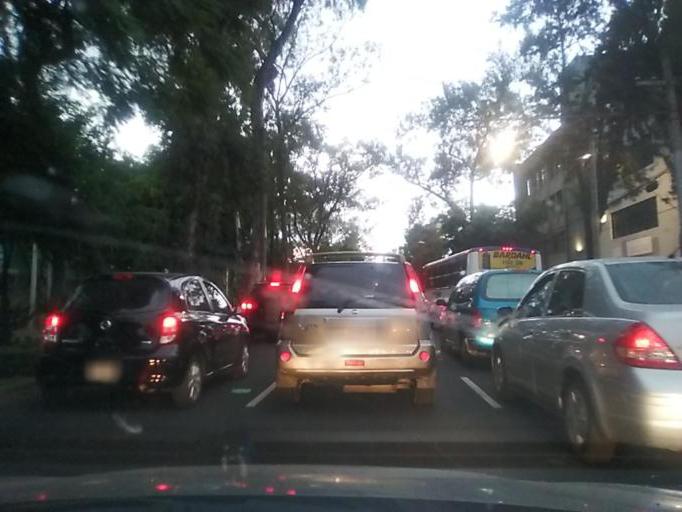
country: MX
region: Mexico City
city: Coyoacan
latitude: 19.3460
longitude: -99.1750
